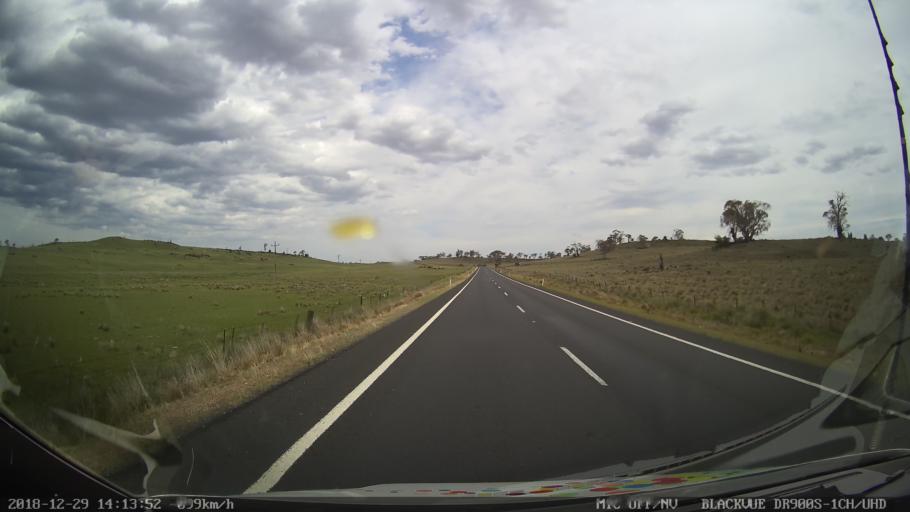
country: AU
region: New South Wales
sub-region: Cooma-Monaro
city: Cooma
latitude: -36.4345
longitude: 149.2381
